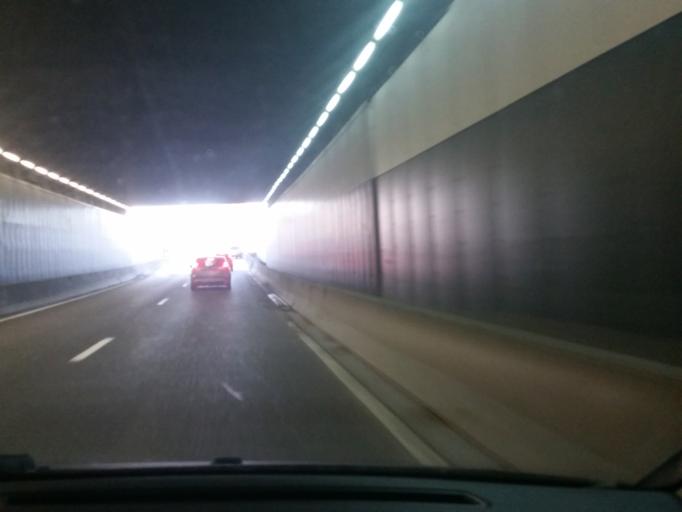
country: BE
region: Flanders
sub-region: Provincie West-Vlaanderen
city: Ostend
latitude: 51.2191
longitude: 2.9373
